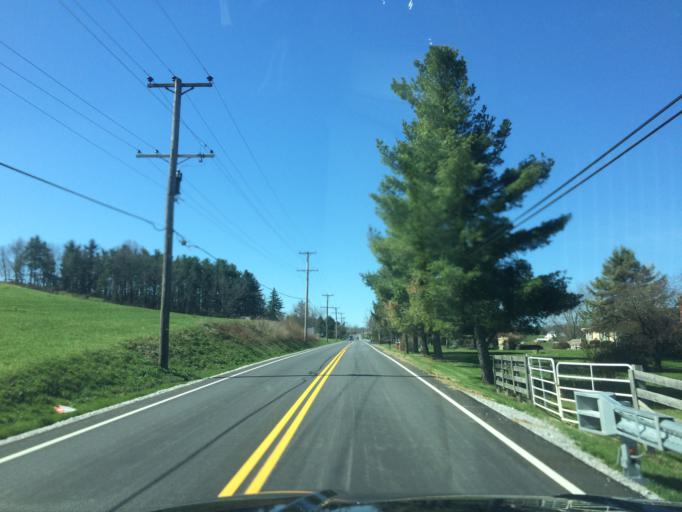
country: US
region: Maryland
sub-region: Carroll County
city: Westminster
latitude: 39.6322
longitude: -76.9907
